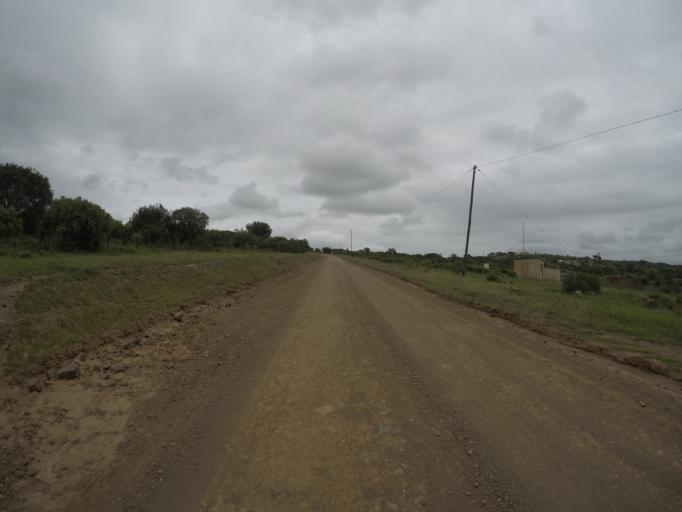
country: ZA
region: KwaZulu-Natal
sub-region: uThungulu District Municipality
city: Empangeni
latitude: -28.6004
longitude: 31.8387
